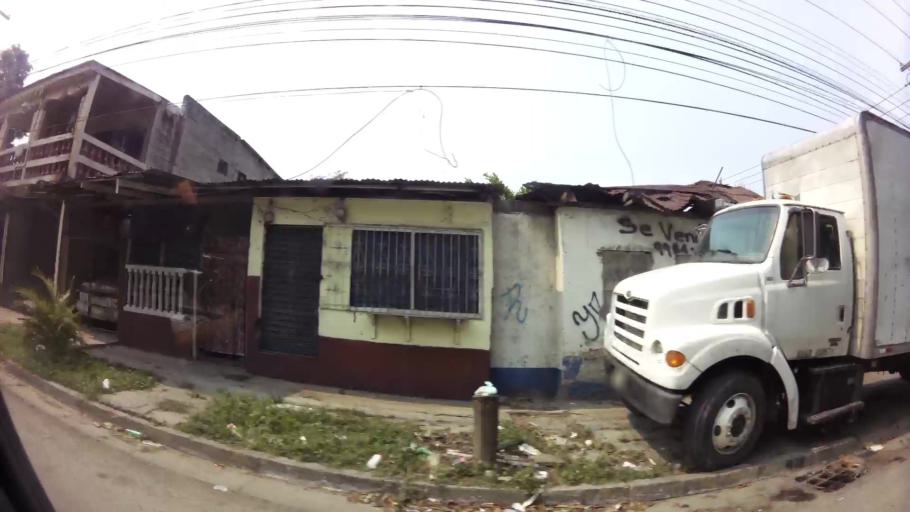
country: HN
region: Cortes
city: San Pedro Sula
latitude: 15.4873
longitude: -88.0221
